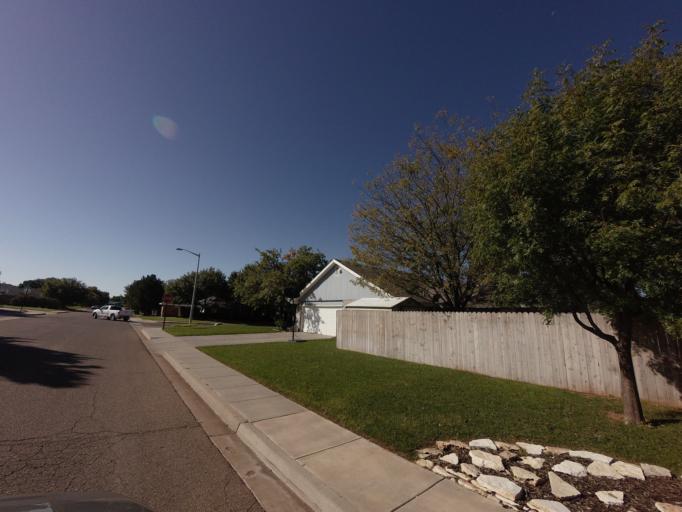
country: US
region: New Mexico
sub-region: Curry County
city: Clovis
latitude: 34.4236
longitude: -103.1703
